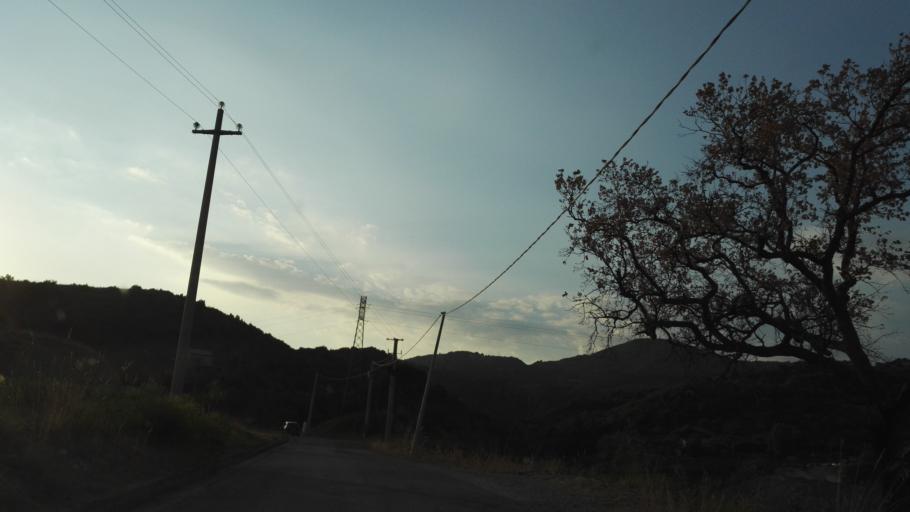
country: IT
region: Calabria
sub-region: Provincia di Reggio Calabria
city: Placanica
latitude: 38.4059
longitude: 16.4277
